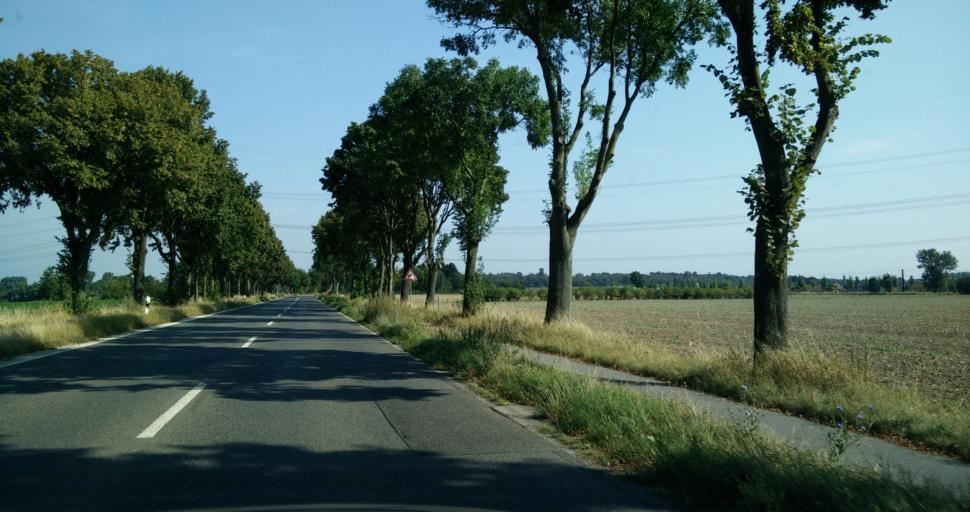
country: DE
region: North Rhine-Westphalia
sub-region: Regierungsbezirk Dusseldorf
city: Hochfeld
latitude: 51.3298
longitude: 6.7463
